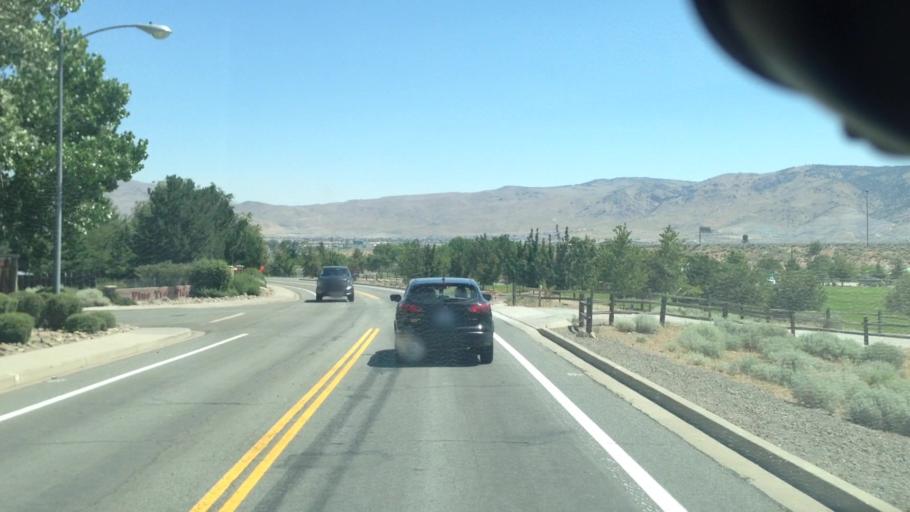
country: US
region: Nevada
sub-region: Washoe County
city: Sparks
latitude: 39.4017
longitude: -119.7613
